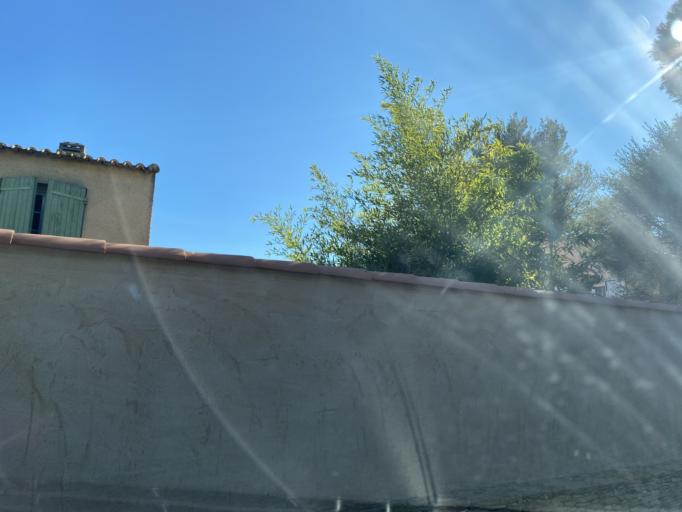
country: FR
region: Provence-Alpes-Cote d'Azur
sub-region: Departement des Bouches-du-Rhone
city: Ceyreste
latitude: 43.2050
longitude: 5.6099
